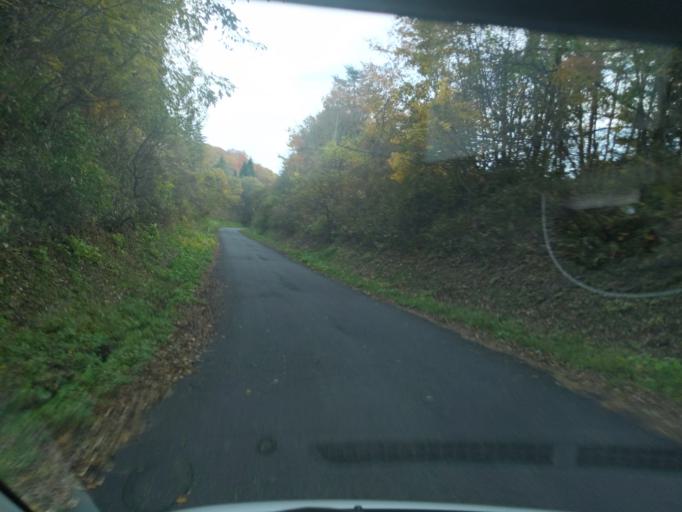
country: JP
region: Iwate
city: Ichinoseki
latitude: 38.9987
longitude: 141.0044
